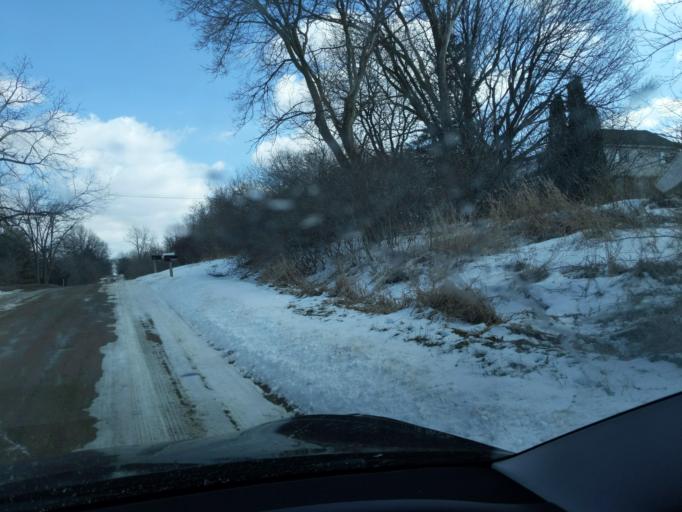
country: US
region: Michigan
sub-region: Livingston County
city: Fowlerville
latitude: 42.6139
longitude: -84.1239
